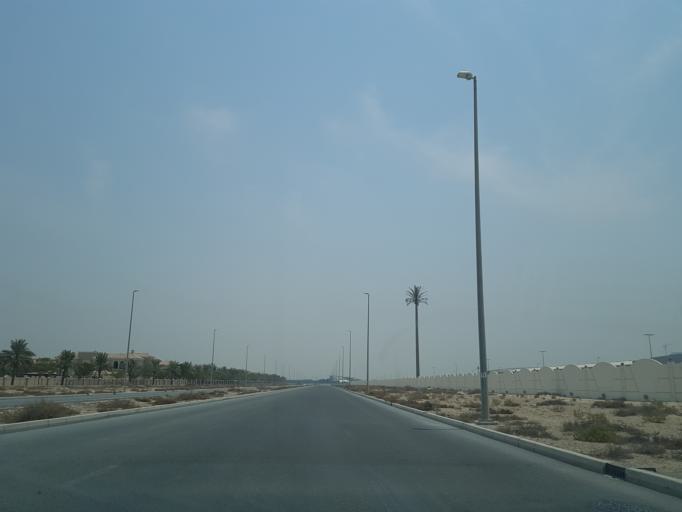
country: AE
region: Dubai
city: Dubai
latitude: 25.0365
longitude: 55.2467
